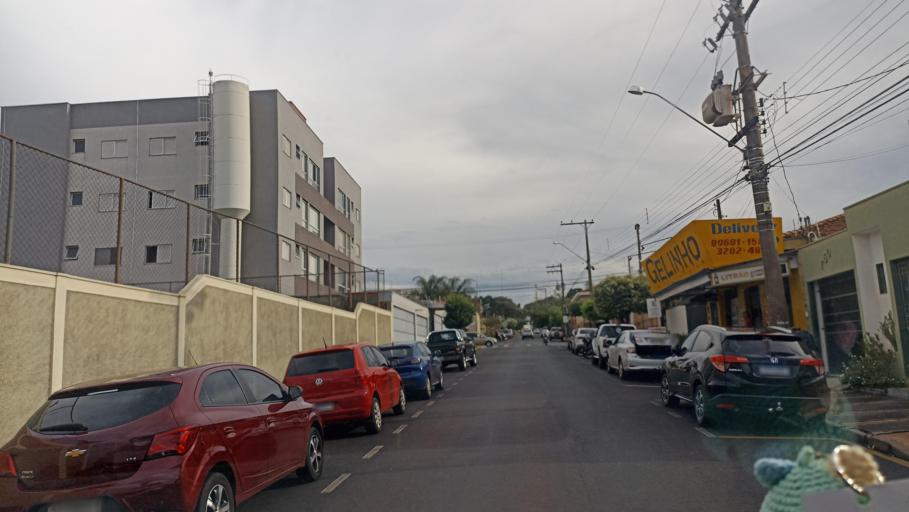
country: BR
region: Sao Paulo
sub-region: Jaboticabal
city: Jaboticabal
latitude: -21.2576
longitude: -48.3245
